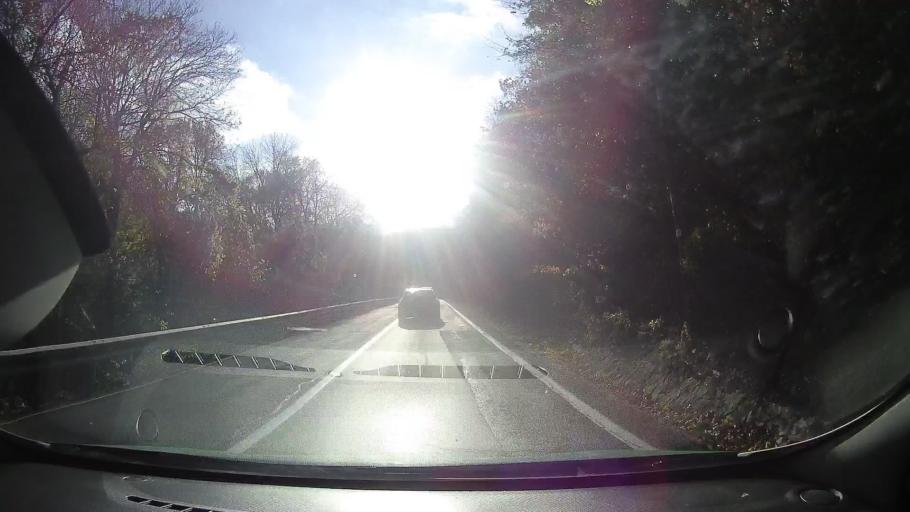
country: RO
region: Tulcea
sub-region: Comuna Topolog
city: Topolog
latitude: 44.9144
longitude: 28.4204
